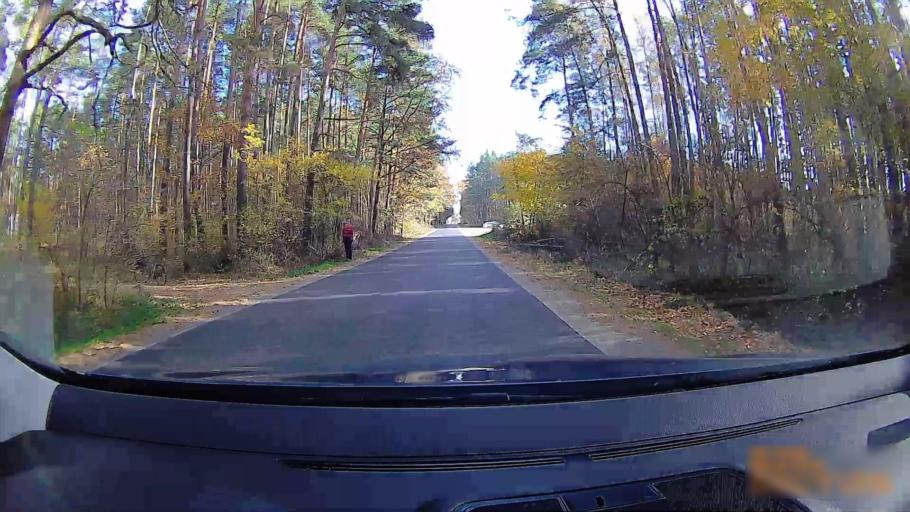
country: PL
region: Greater Poland Voivodeship
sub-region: Powiat ostrzeszowski
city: Doruchow
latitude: 51.4054
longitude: 18.0177
